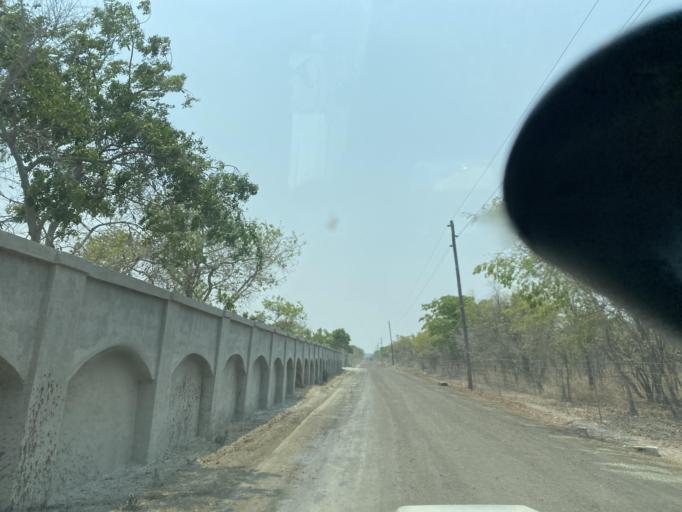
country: ZM
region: Lusaka
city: Lusaka
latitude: -15.5254
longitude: 28.4441
